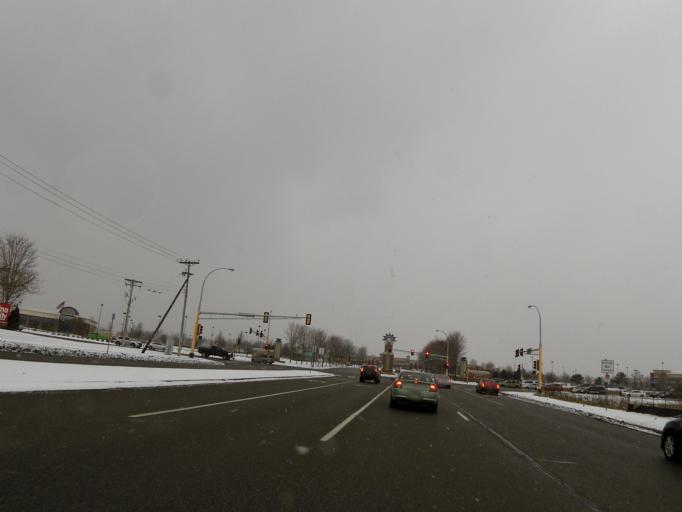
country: US
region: Minnesota
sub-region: Washington County
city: Woodbury
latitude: 44.9416
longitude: -92.9328
